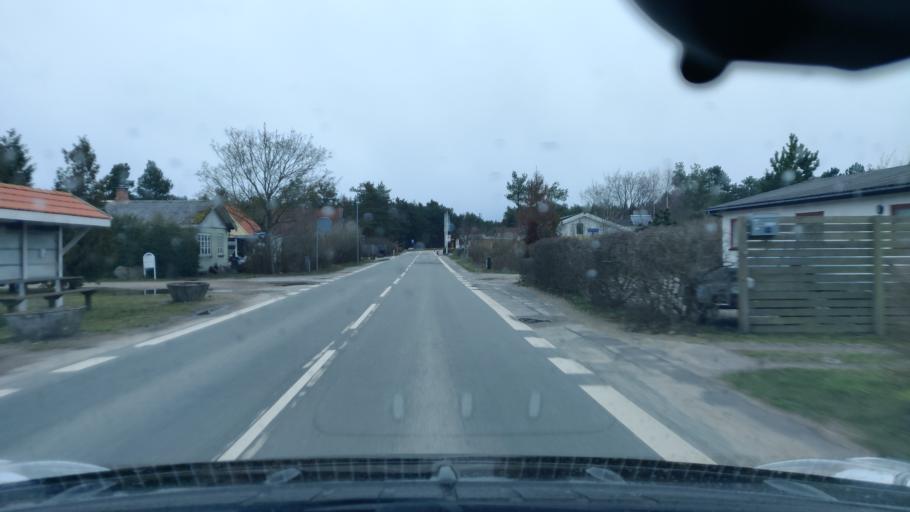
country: DK
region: Zealand
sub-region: Odsherred Kommune
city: Hojby
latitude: 55.8836
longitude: 11.5494
